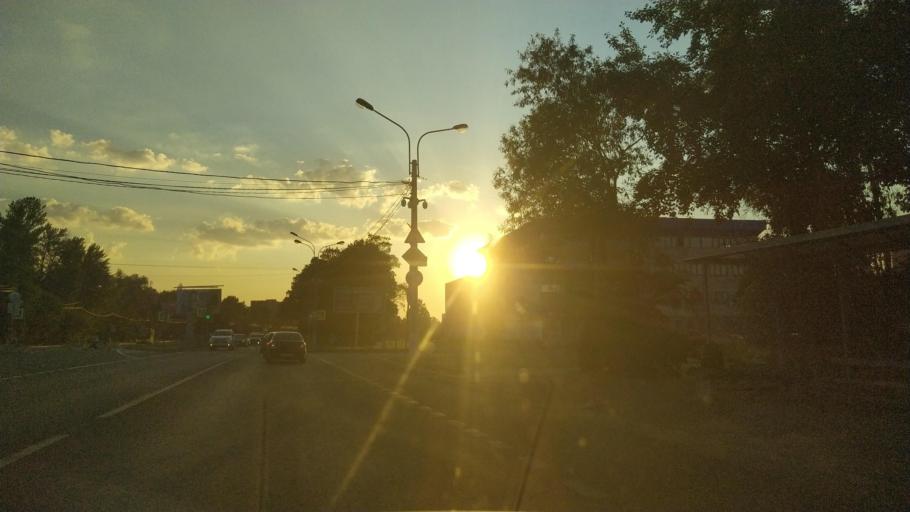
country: RU
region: St.-Petersburg
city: Kronshtadt
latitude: 60.0066
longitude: 29.7423
